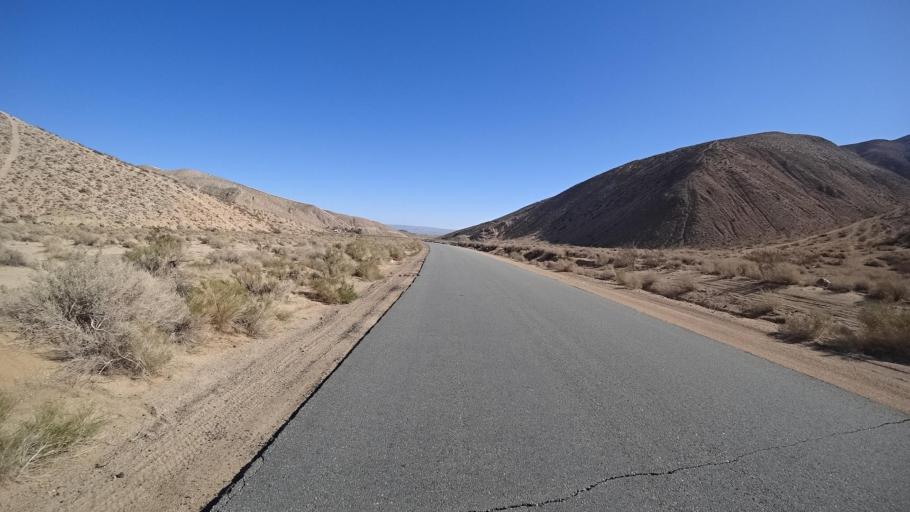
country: US
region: California
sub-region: Kern County
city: California City
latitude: 35.3142
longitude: -118.0598
